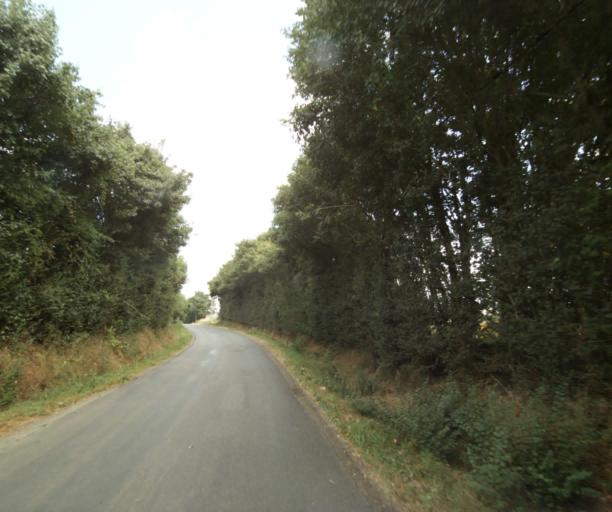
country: FR
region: Pays de la Loire
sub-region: Departement de la Sarthe
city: Auvers-le-Hamon
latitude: 47.8652
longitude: -0.3596
